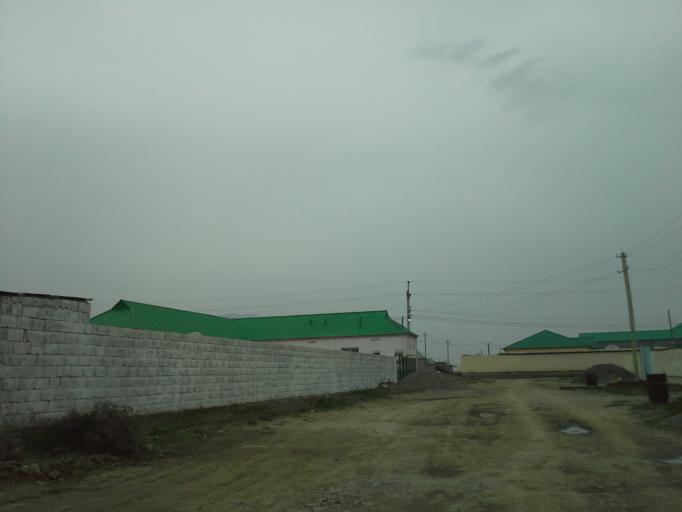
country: TM
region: Ahal
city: Abadan
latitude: 37.9796
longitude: 58.2212
